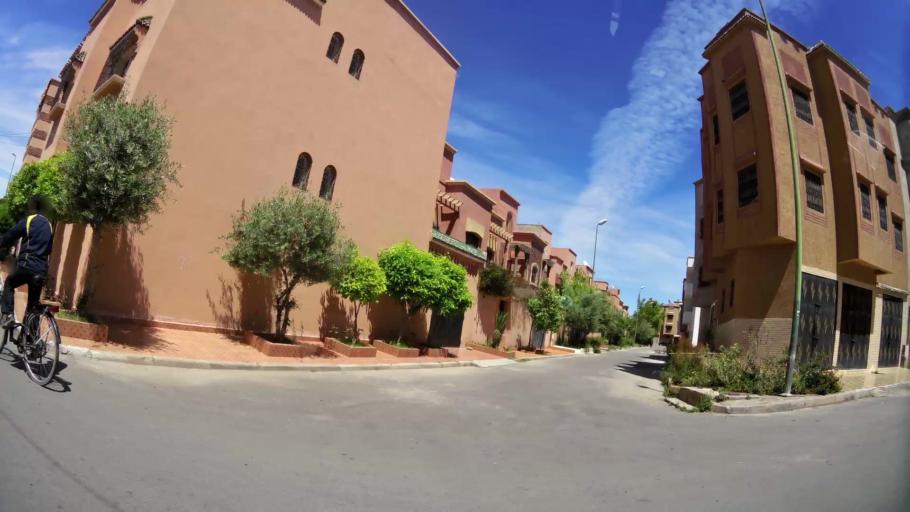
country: MA
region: Marrakech-Tensift-Al Haouz
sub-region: Marrakech
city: Marrakesh
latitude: 31.6413
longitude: -8.0512
